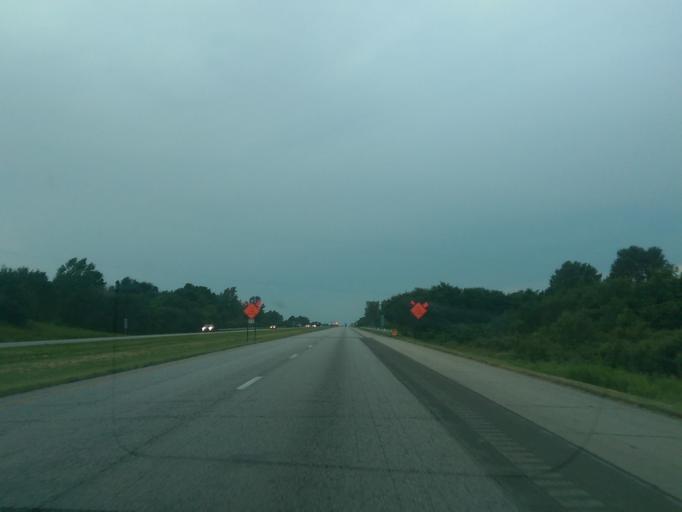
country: US
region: Missouri
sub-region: Holt County
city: Oregon
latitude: 40.0363
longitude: -95.1221
